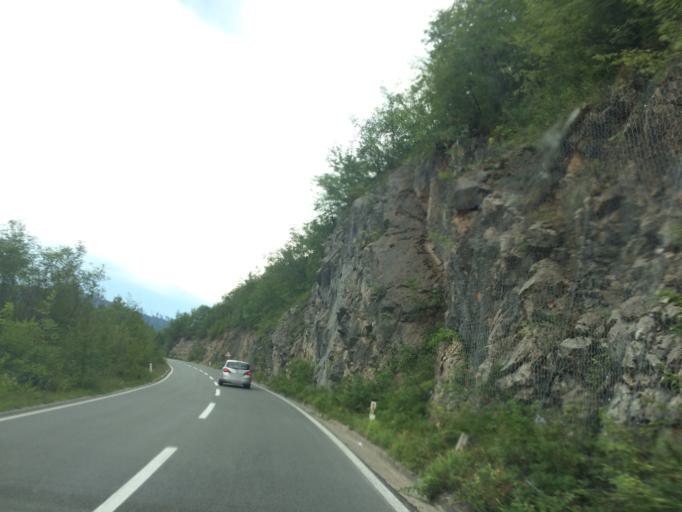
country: ME
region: Opstina Zabljak
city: Zabljak
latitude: 43.1505
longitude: 19.2845
